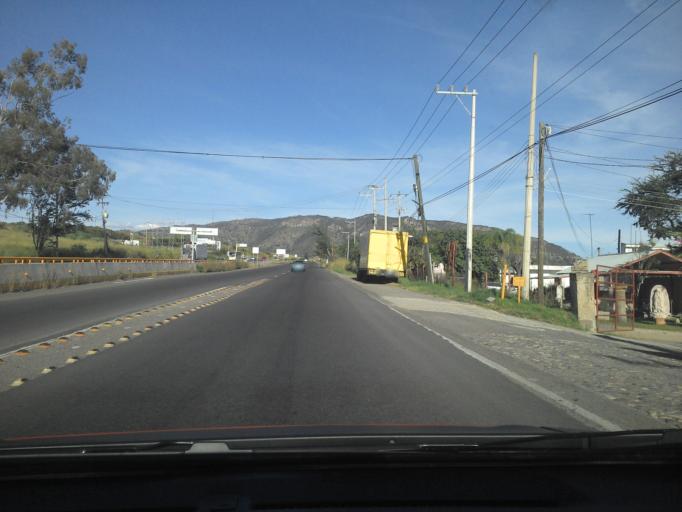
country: MX
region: Jalisco
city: La Venta del Astillero
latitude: 20.7324
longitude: -103.6037
